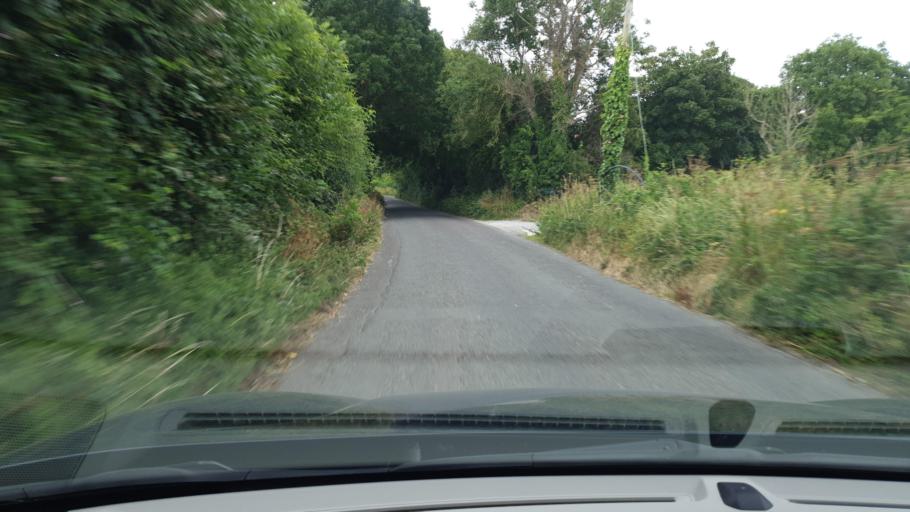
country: IE
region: Leinster
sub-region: An Mhi
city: Stamullin
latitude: 53.5834
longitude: -6.3129
